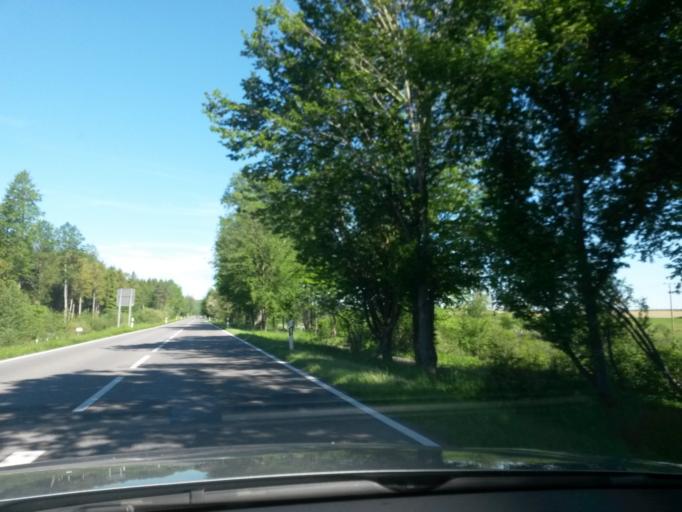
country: DE
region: Baden-Wuerttemberg
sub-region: Tuebingen Region
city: Durnau
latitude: 48.0679
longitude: 9.5725
